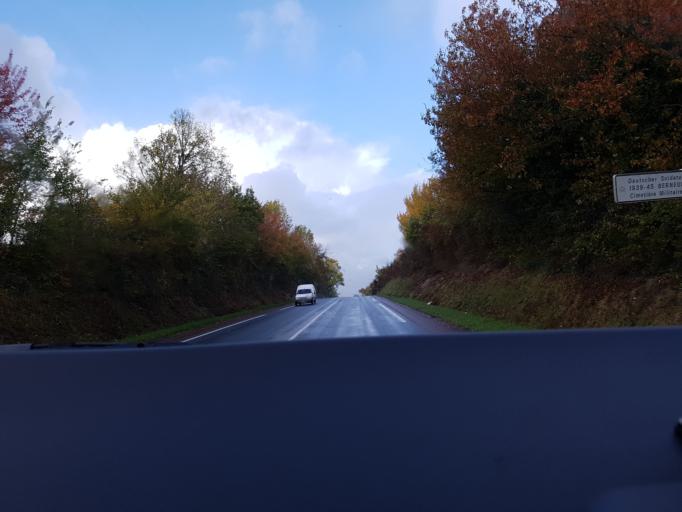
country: FR
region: Poitou-Charentes
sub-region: Departement de la Charente-Maritime
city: Les Gonds
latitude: 45.6775
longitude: -0.6056
